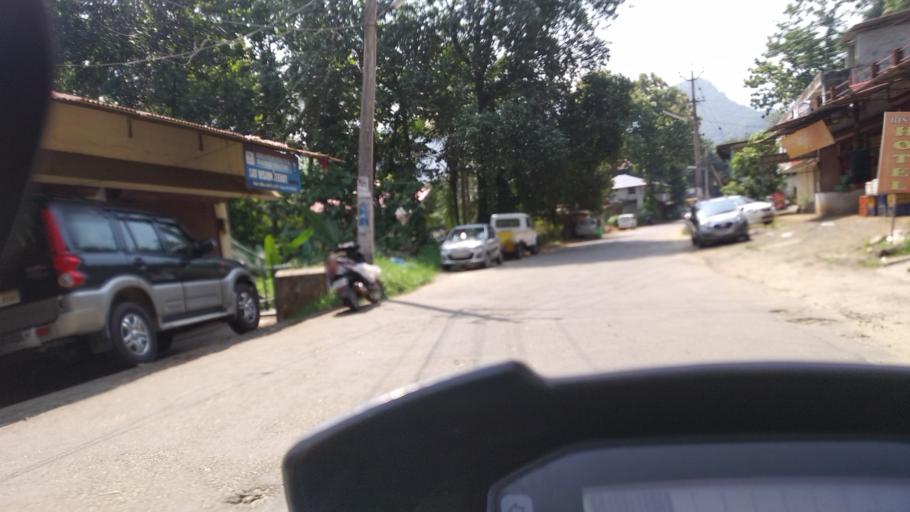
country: IN
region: Kerala
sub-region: Kottayam
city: Erattupetta
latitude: 9.6992
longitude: 76.8197
